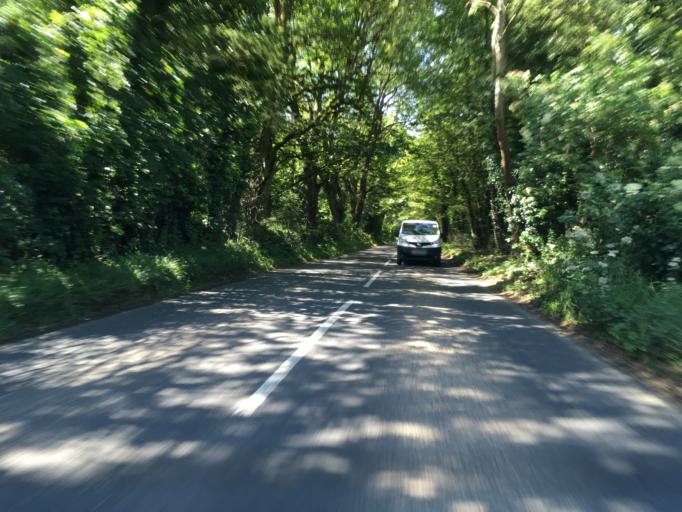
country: GB
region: England
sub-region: Gloucestershire
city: Westfield
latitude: 51.9093
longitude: -1.8072
